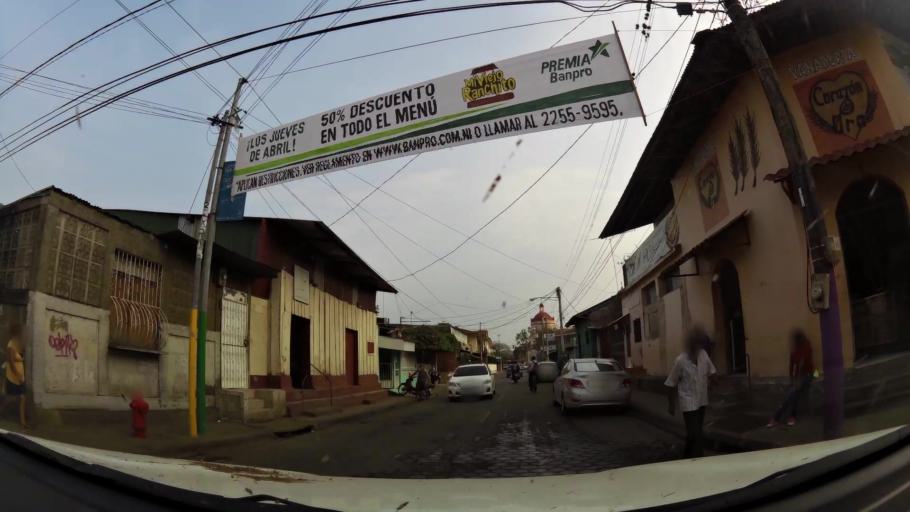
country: NI
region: Masaya
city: Masaya
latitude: 11.9806
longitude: -86.0972
